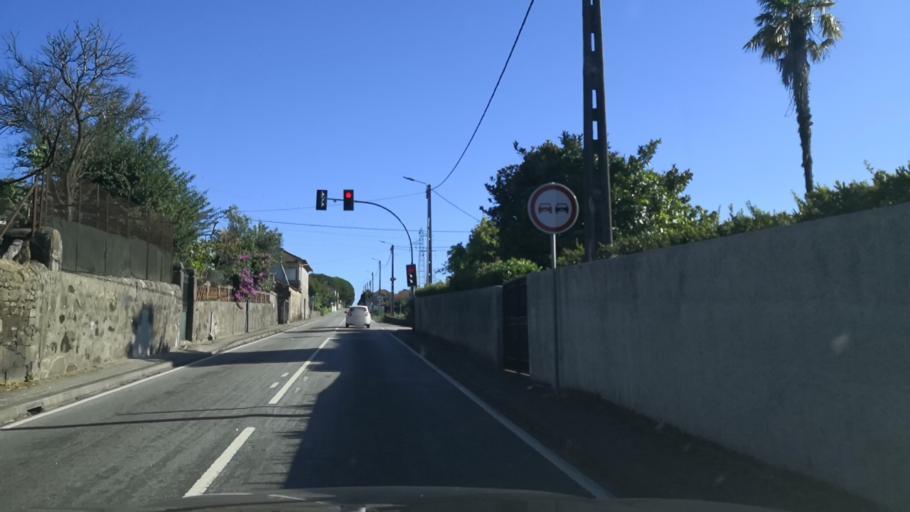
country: PT
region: Porto
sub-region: Santo Tirso
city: Sao Miguel do Couto
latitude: 41.3012
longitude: -8.4710
